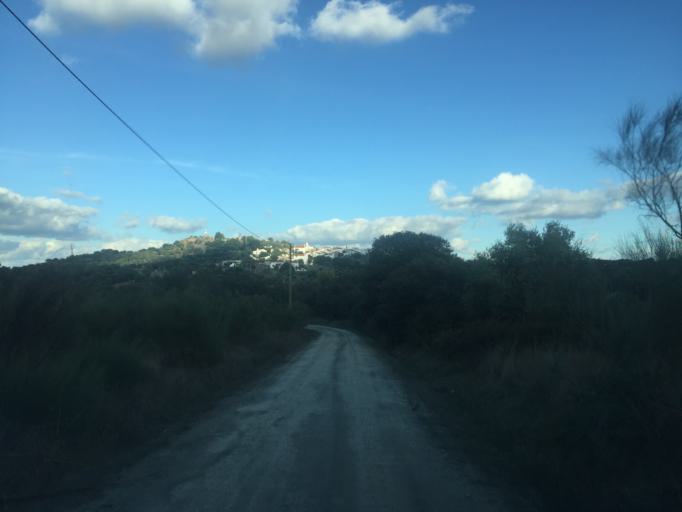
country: PT
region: Portalegre
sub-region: Alter do Chao
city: Alter do Chao
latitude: 39.1858
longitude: -7.6304
